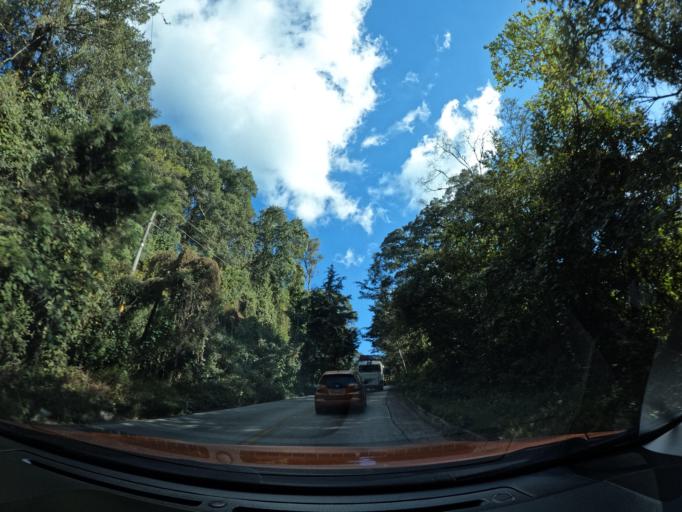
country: GT
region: Sacatepequez
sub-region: Municipio de Santa Maria de Jesus
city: Santa Maria de Jesus
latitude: 14.5082
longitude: -90.7173
